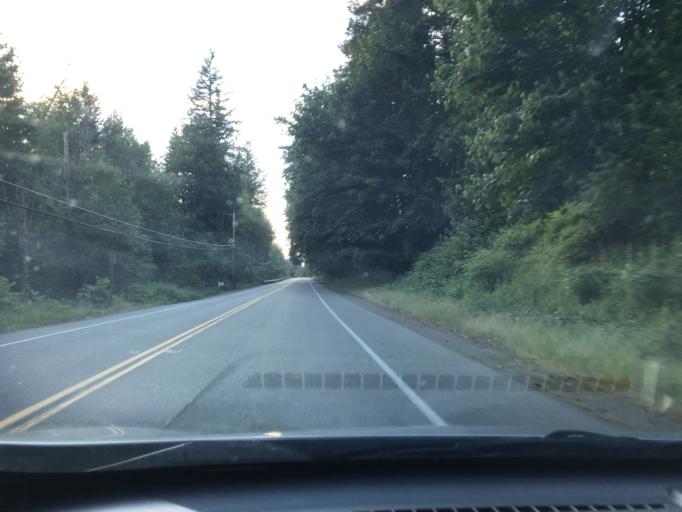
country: US
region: Washington
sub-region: King County
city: Lake Morton-Berrydale
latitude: 47.3087
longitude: -122.0899
